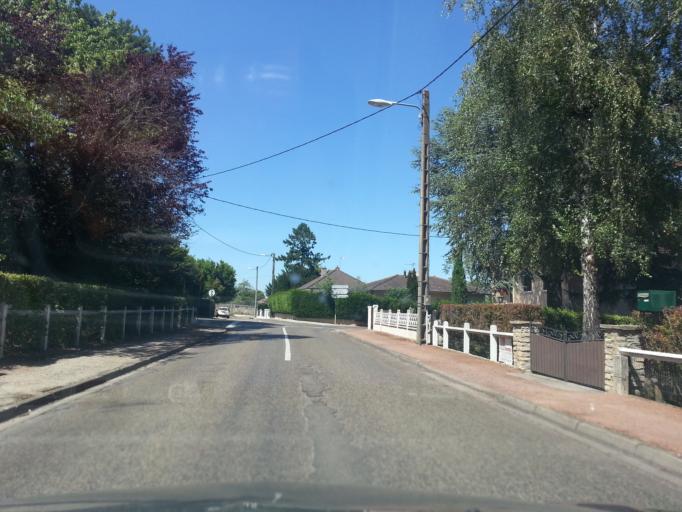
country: FR
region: Bourgogne
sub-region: Departement de Saone-et-Loire
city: Chatenoy-le-Royal
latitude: 46.7892
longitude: 4.8125
